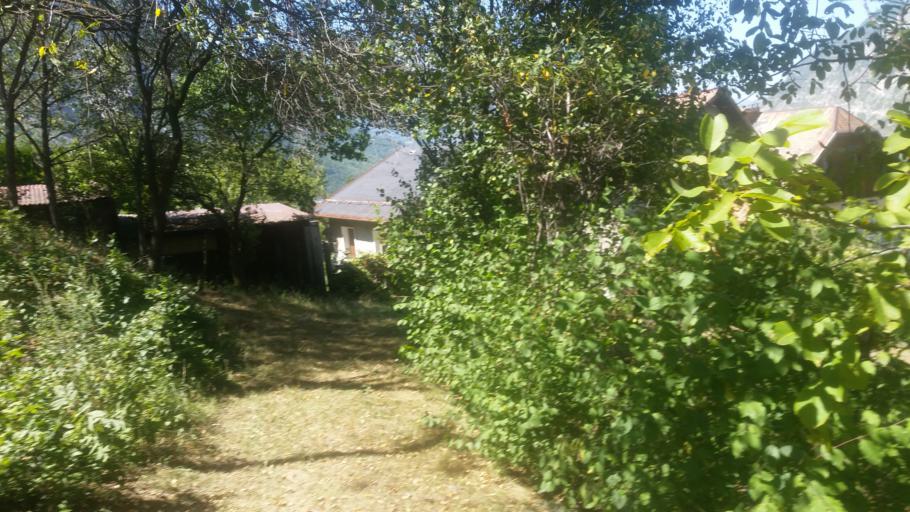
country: FR
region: Rhone-Alpes
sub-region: Departement de la Savoie
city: Villargondran
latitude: 45.2467
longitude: 6.4003
